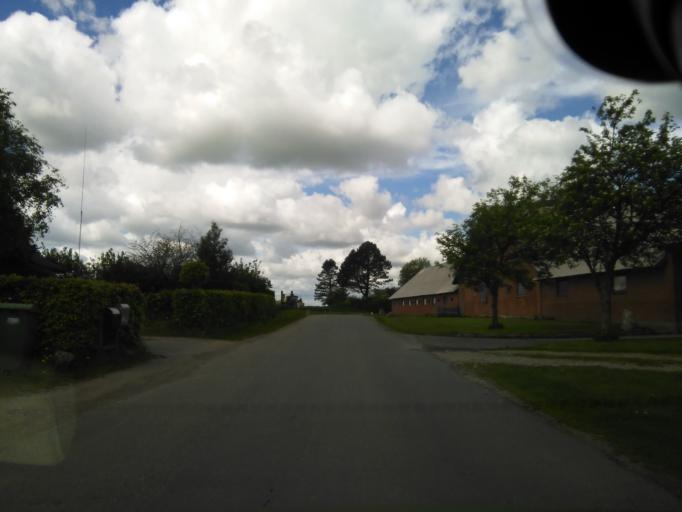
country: DK
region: Central Jutland
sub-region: Arhus Kommune
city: Solbjerg
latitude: 56.0200
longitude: 10.1183
